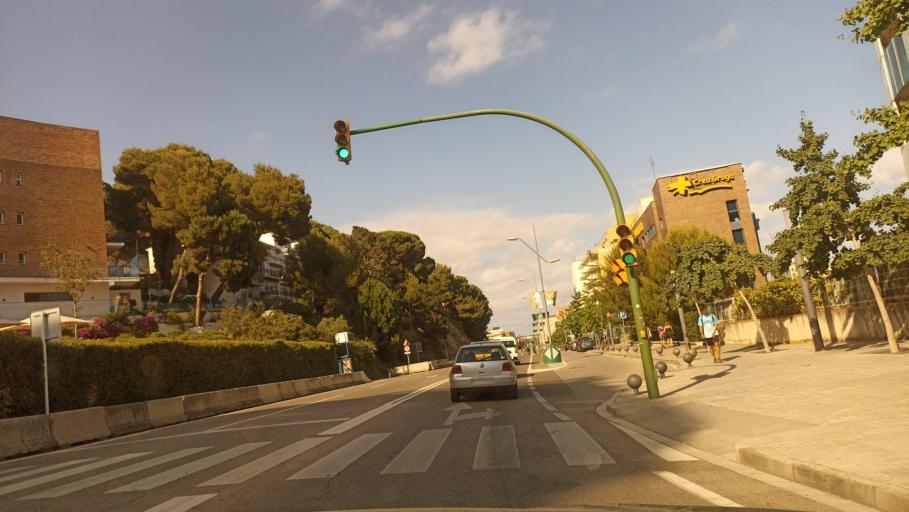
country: ES
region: Catalonia
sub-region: Provincia de Barcelona
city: Calella
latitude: 41.6109
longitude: 2.6475
